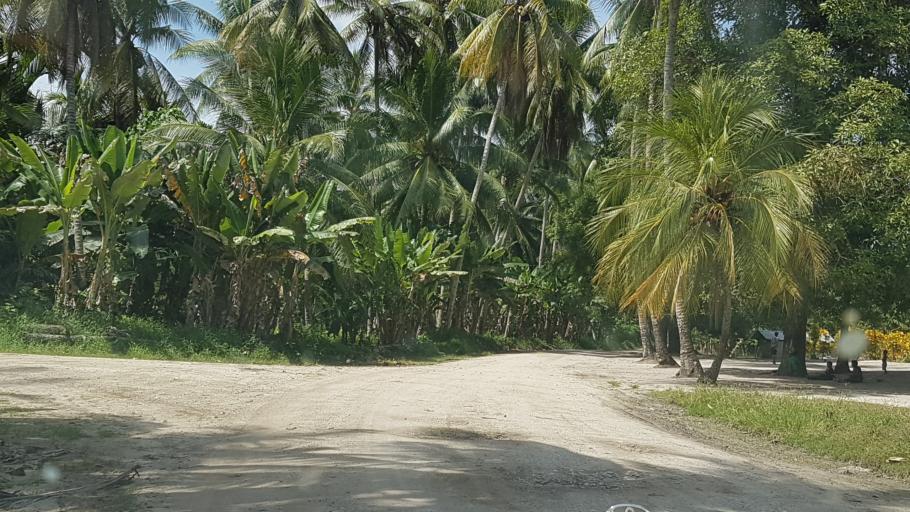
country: PG
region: East Sepik
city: Angoram
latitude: -4.2283
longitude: 144.9328
